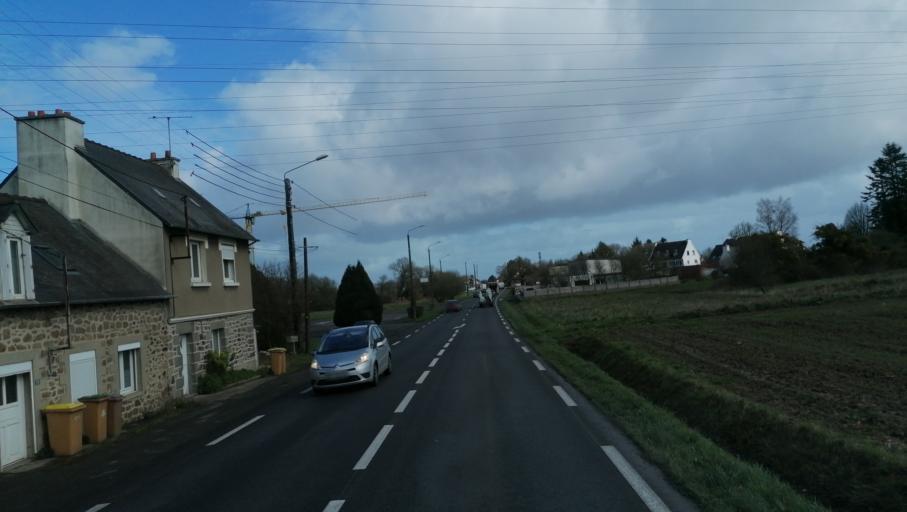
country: FR
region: Brittany
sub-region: Departement des Cotes-d'Armor
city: Ploufragan
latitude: 48.4739
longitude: -2.8003
